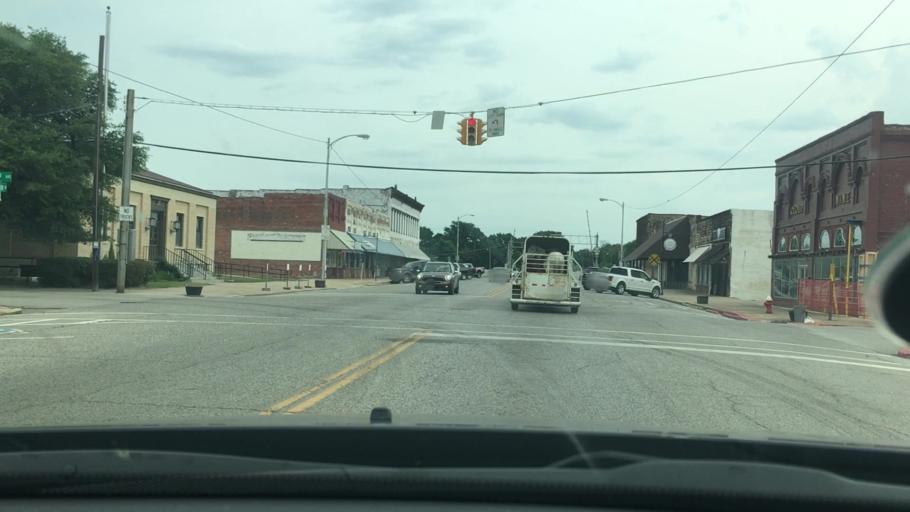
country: US
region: Oklahoma
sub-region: Love County
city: Marietta
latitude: 33.9373
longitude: -97.1184
